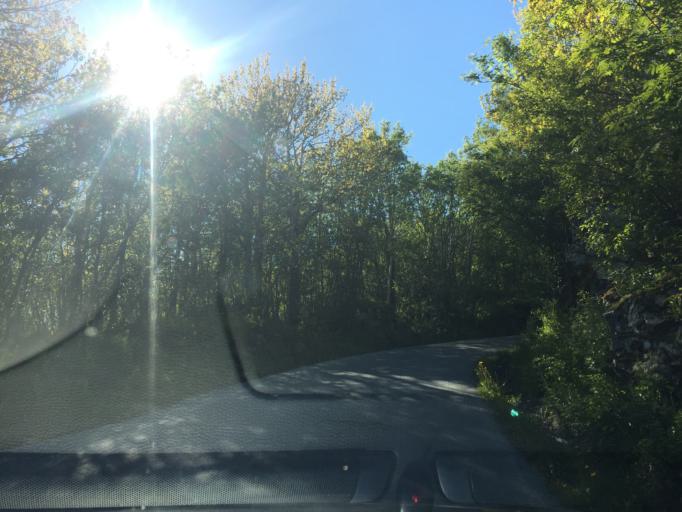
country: NO
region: Nordland
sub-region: Bodo
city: Loding
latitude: 67.4054
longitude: 14.6320
